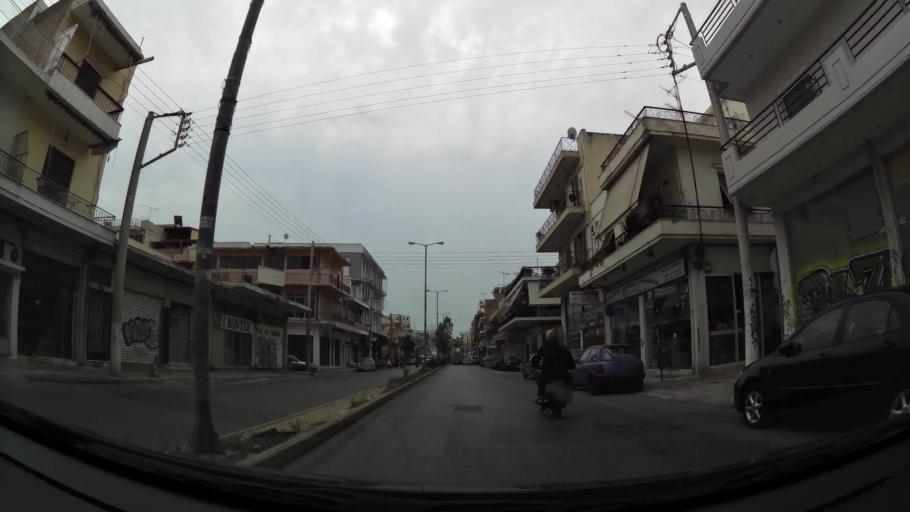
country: GR
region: Attica
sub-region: Nomos Piraios
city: Agios Ioannis Rentis
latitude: 37.9648
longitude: 23.6593
